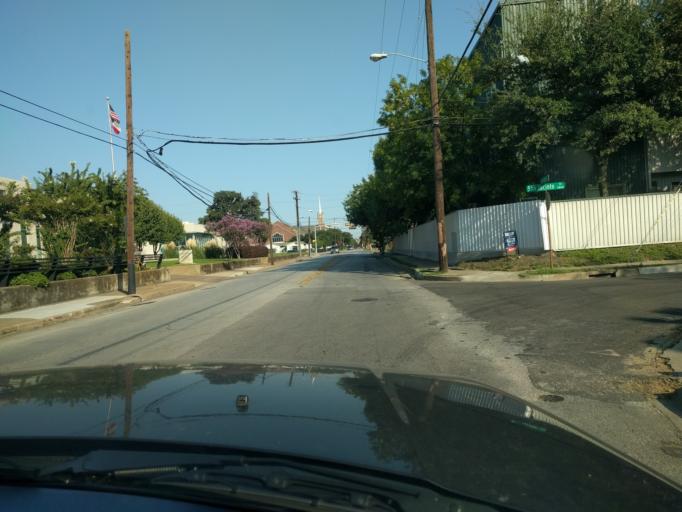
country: US
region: Texas
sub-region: Dallas County
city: Dallas
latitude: 32.7971
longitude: -96.7852
